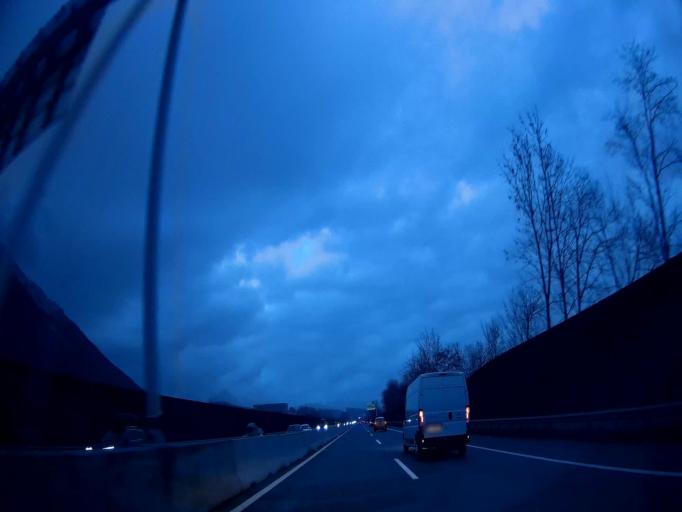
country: AT
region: Salzburg
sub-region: Politischer Bezirk Salzburg-Umgebung
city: Grodig
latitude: 47.7439
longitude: 13.0365
